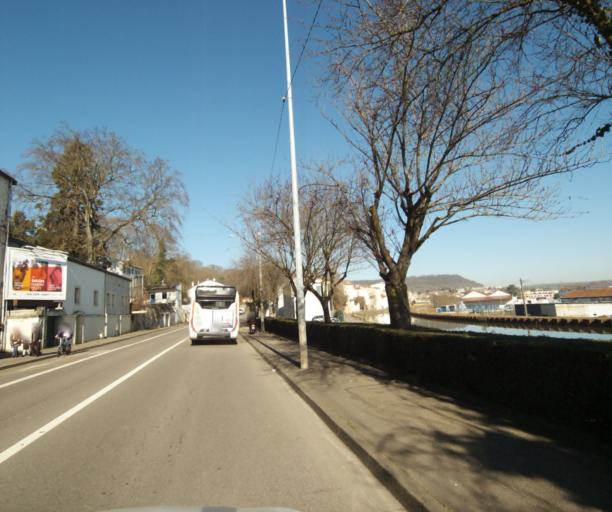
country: FR
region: Lorraine
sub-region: Departement de Meurthe-et-Moselle
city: Maxeville
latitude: 48.7062
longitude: 6.1678
